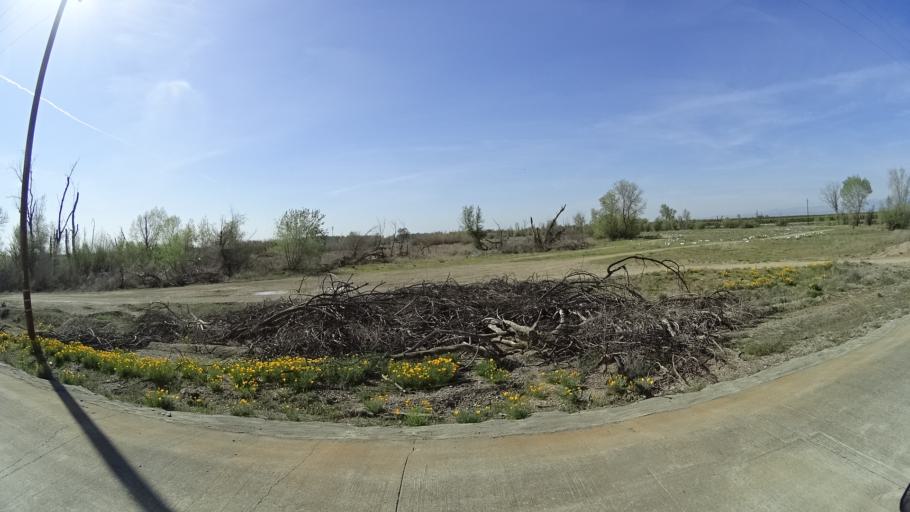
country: US
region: California
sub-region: Glenn County
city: Willows
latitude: 39.6117
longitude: -122.2005
